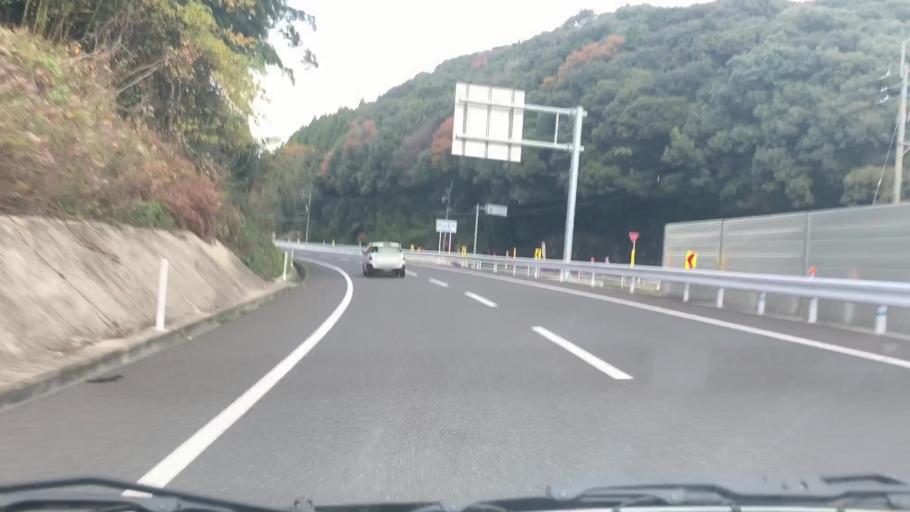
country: JP
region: Saga Prefecture
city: Takeocho-takeo
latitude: 33.2617
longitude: 129.9718
